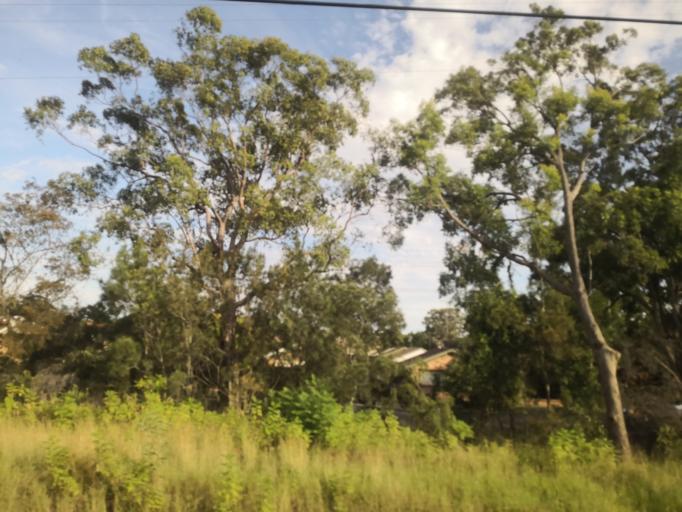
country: AU
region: New South Wales
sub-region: Gosford Shire
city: Blackwall
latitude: -33.4960
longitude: 151.3096
